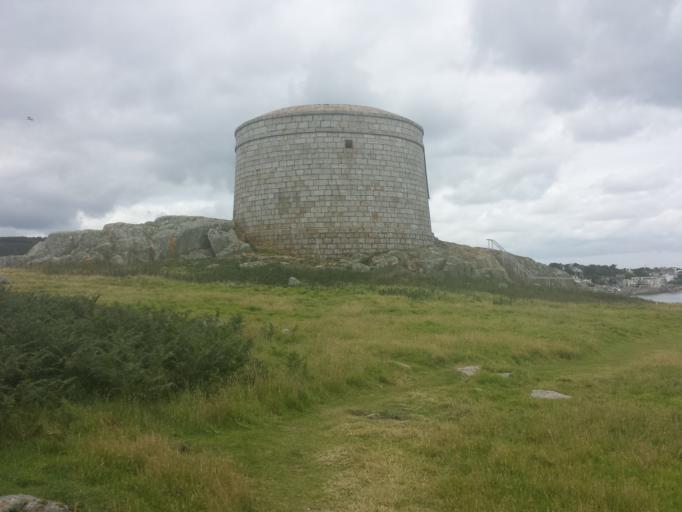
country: IE
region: Leinster
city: Dalkey
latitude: 53.2715
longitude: -6.0844
